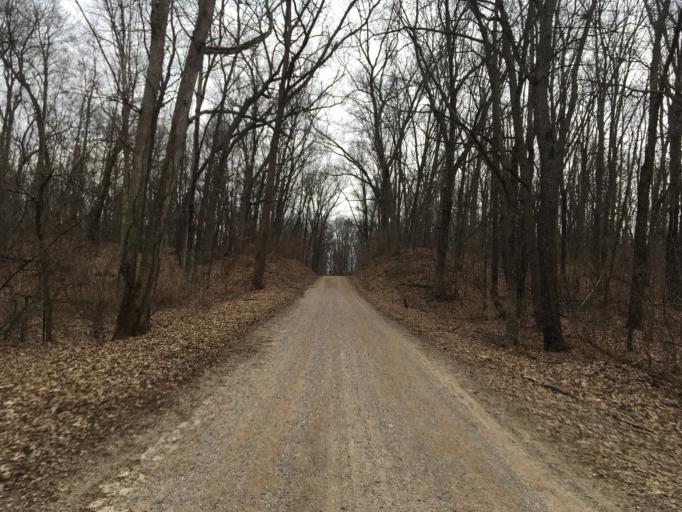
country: US
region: Michigan
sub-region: Jackson County
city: Grass Lake
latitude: 42.3227
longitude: -84.1950
